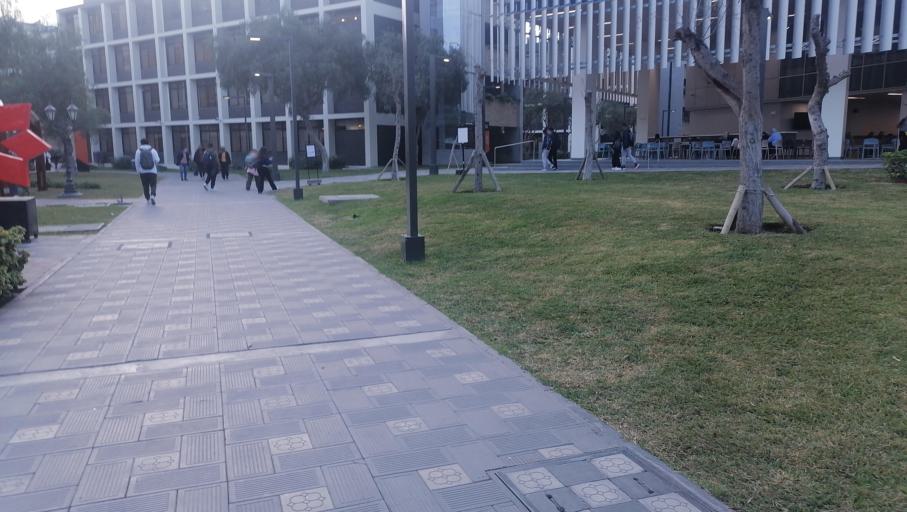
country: PE
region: Lima
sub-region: Lima
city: La Molina
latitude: -12.0848
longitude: -76.9712
